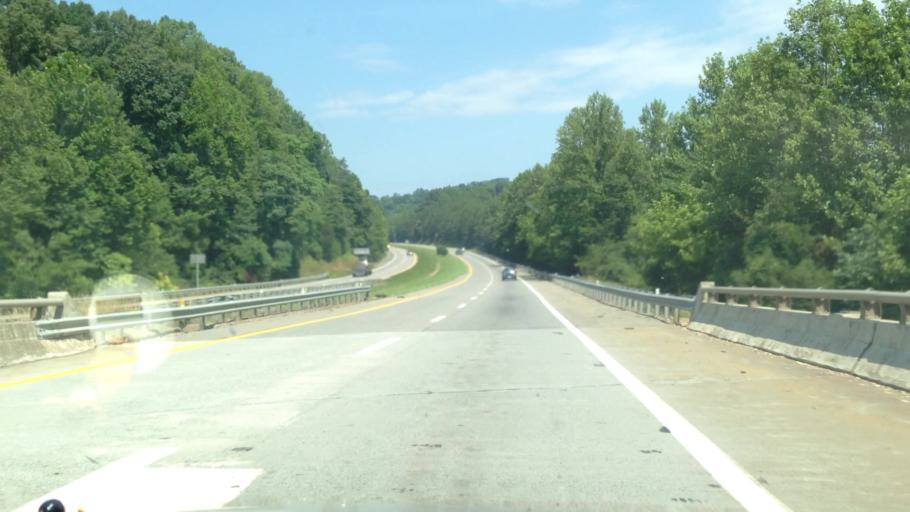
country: US
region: Virginia
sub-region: Henry County
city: Collinsville
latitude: 36.6848
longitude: -79.9395
